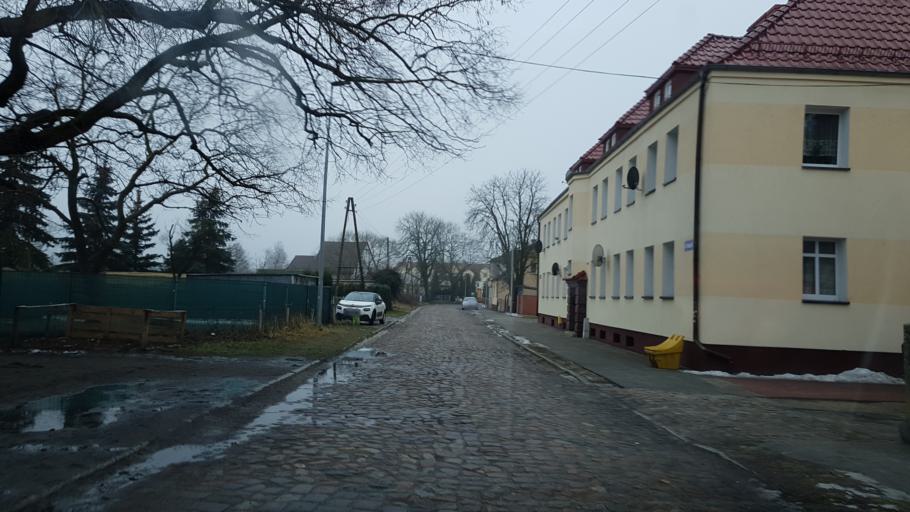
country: PL
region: West Pomeranian Voivodeship
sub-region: Szczecin
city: Szczecin
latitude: 53.3965
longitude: 14.6877
